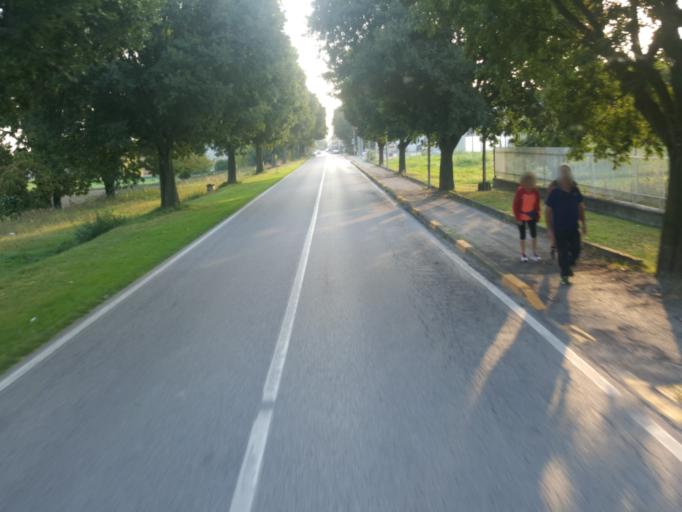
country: IT
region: Emilia-Romagna
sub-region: Provincia di Ravenna
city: Voltana
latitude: 44.5872
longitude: 11.9248
